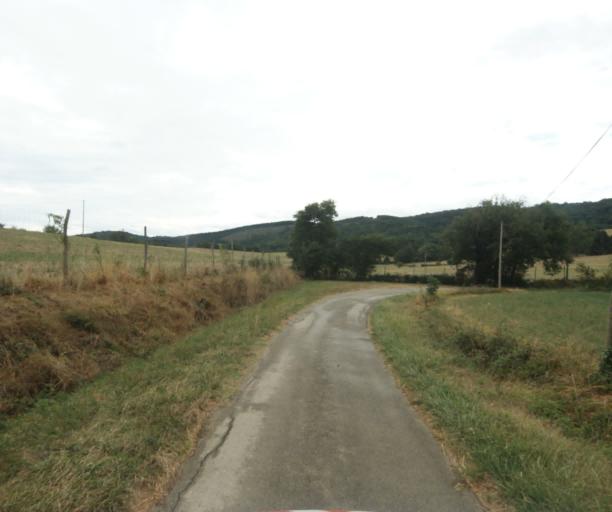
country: FR
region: Midi-Pyrenees
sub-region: Departement de la Haute-Garonne
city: Revel
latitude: 43.4252
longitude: 1.9981
